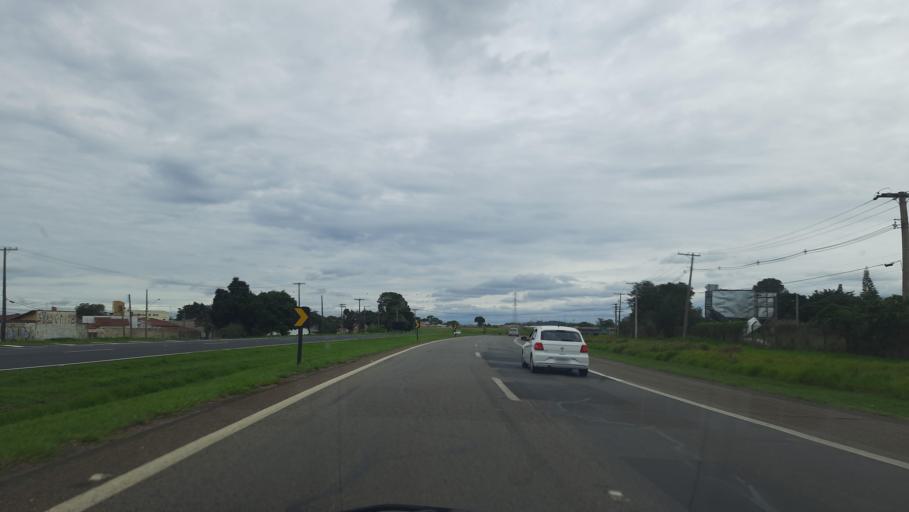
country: BR
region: Sao Paulo
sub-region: Moji-Guacu
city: Mogi-Gaucu
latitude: -22.3452
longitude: -46.9566
